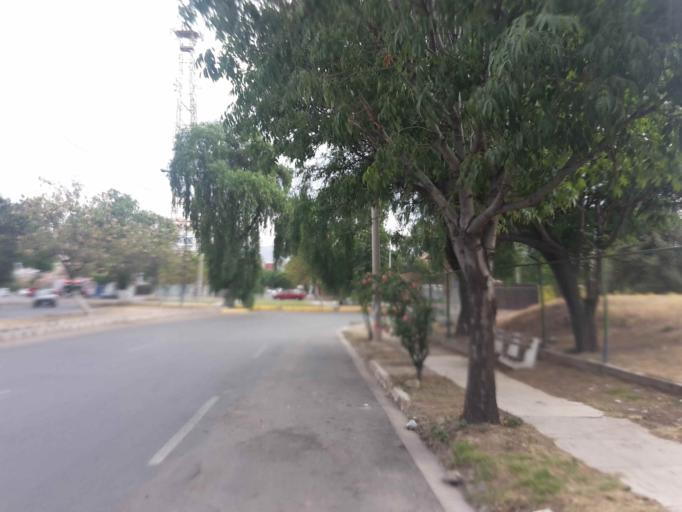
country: BO
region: Cochabamba
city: Cochabamba
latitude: -17.3618
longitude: -66.1733
